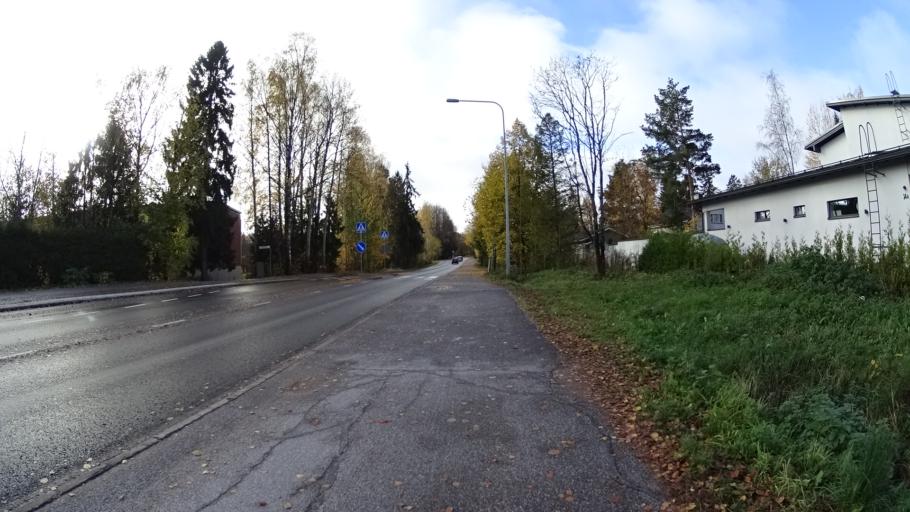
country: FI
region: Uusimaa
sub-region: Helsinki
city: Kauniainen
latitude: 60.2274
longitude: 24.7079
